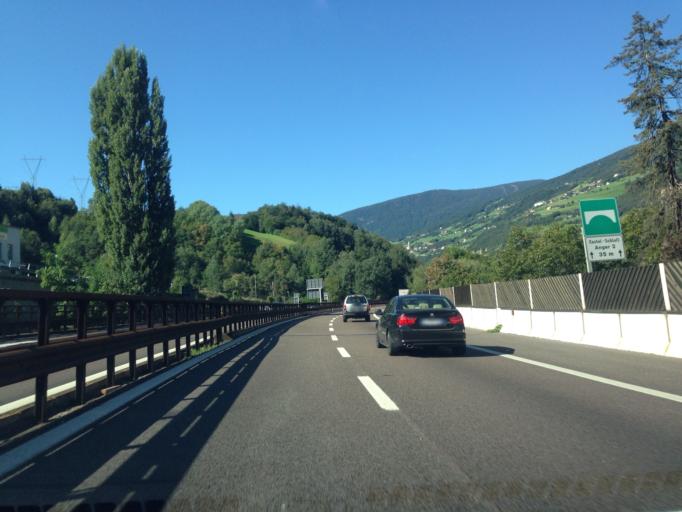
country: IT
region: Trentino-Alto Adige
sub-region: Bolzano
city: Chiusa
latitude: 46.6438
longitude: 11.5842
